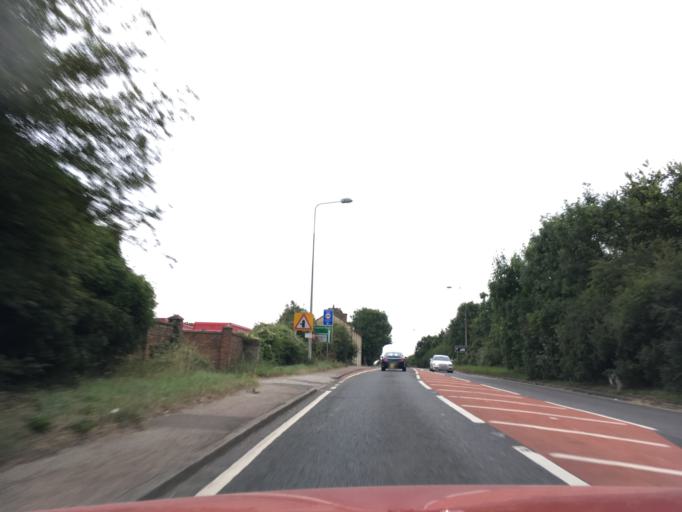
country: GB
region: England
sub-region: Central Bedfordshire
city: Hockliffe
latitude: 51.9251
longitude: -0.5772
